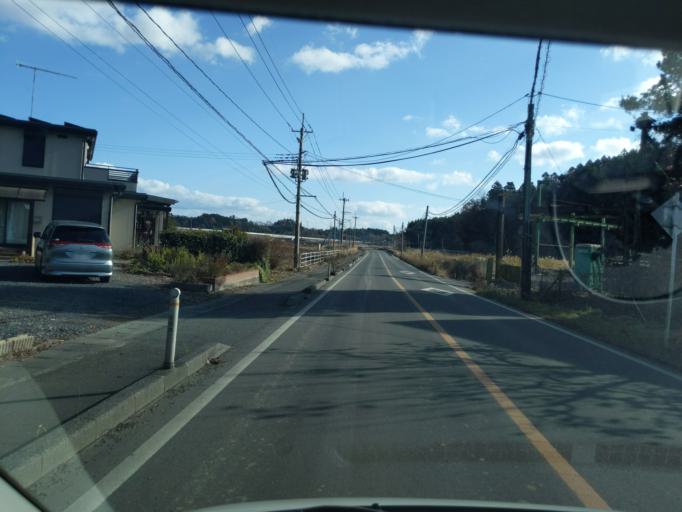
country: JP
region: Miyagi
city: Kogota
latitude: 38.7323
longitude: 141.0479
